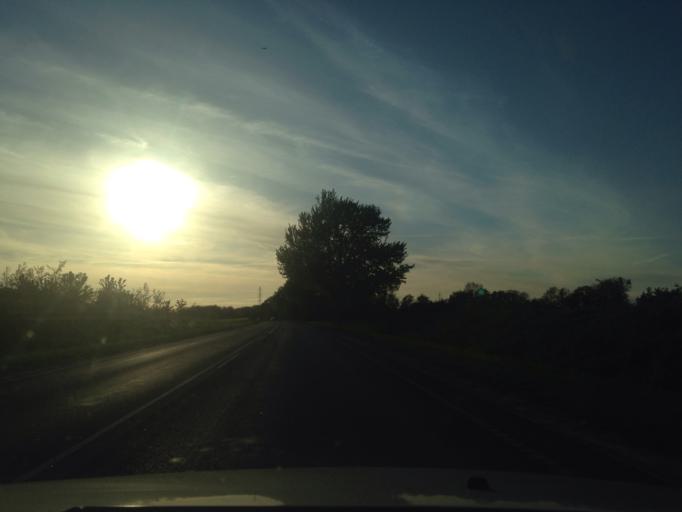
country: DK
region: Zealand
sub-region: Greve Kommune
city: Tune
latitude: 55.6013
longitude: 12.2214
